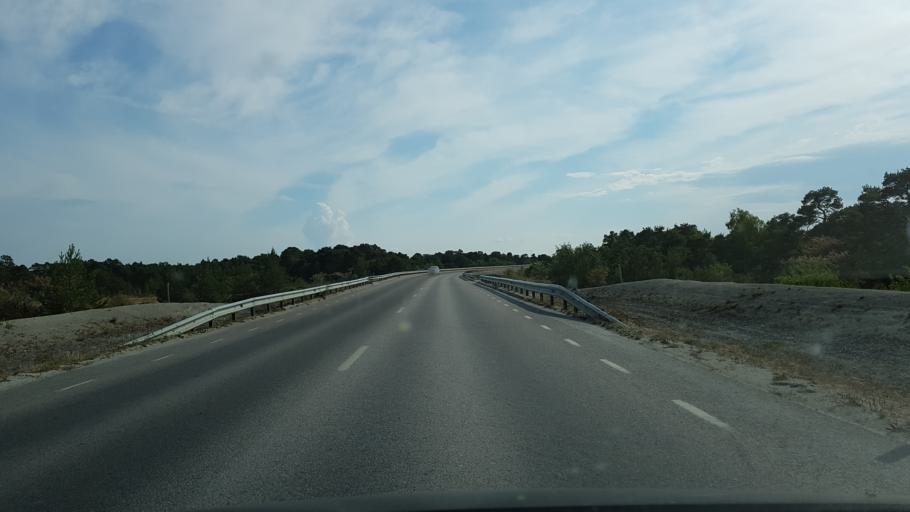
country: SE
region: Gotland
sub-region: Gotland
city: Visby
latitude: 57.6345
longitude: 18.3595
